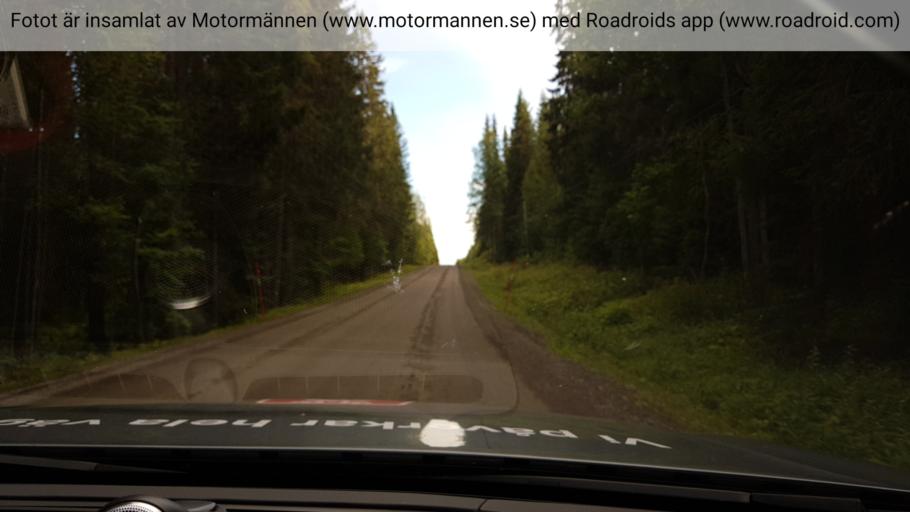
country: SE
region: Jaemtland
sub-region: Stroemsunds Kommun
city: Stroemsund
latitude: 64.0019
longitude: 15.8166
